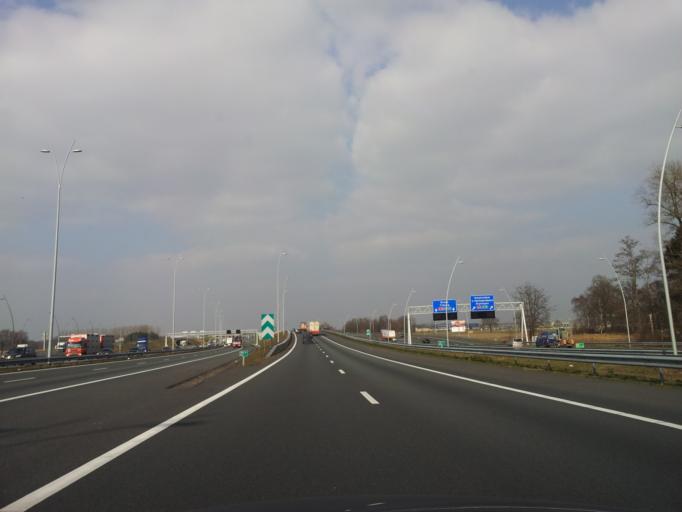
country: NL
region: North Brabant
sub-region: Gemeente Eindhoven
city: Meerhoven
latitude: 51.4704
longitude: 5.4048
